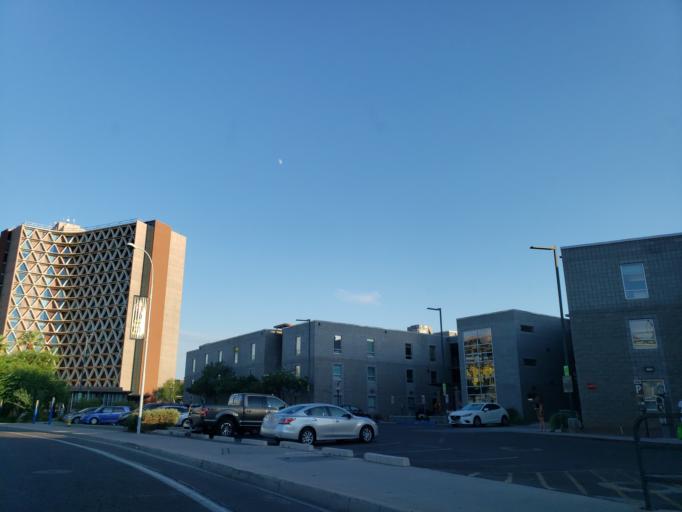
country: US
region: Arizona
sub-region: Maricopa County
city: Tempe Junction
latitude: 33.4234
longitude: -111.9314
